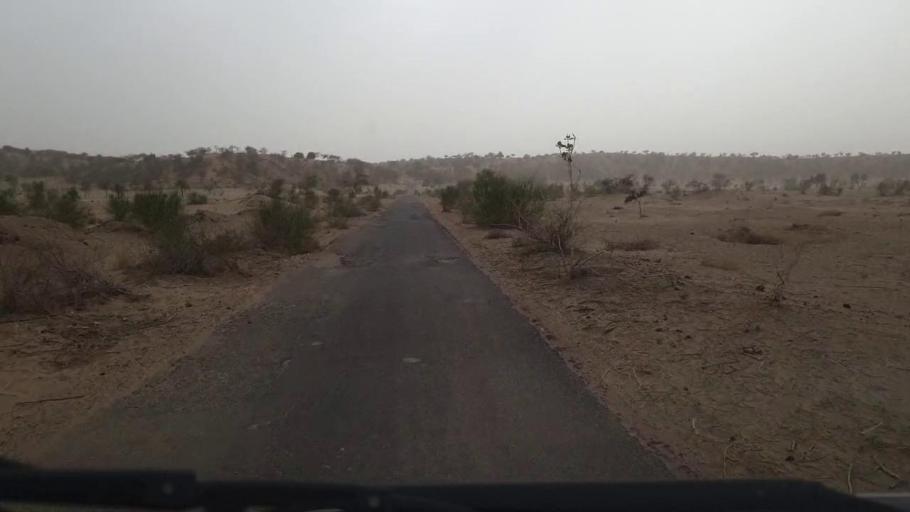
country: PK
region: Sindh
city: Islamkot
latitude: 25.0660
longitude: 70.5484
